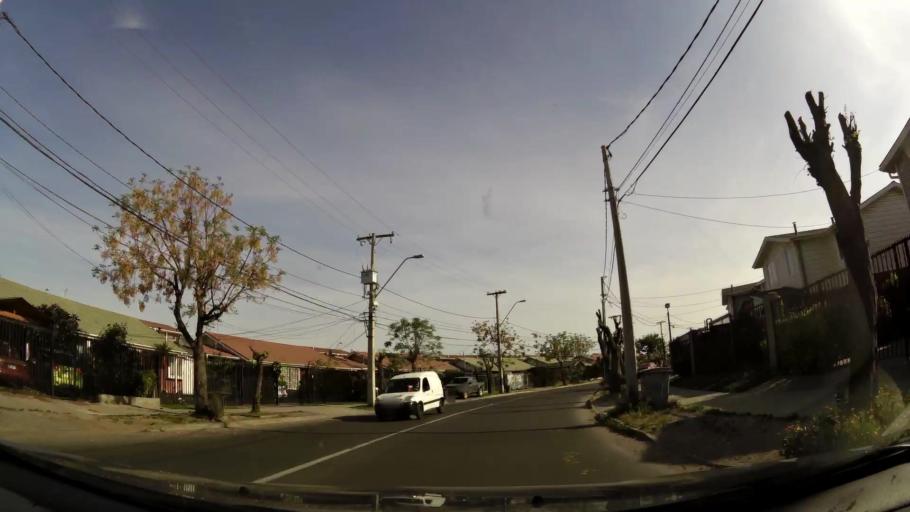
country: CL
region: Santiago Metropolitan
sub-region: Provincia de Cordillera
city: Puente Alto
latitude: -33.5916
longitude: -70.5559
